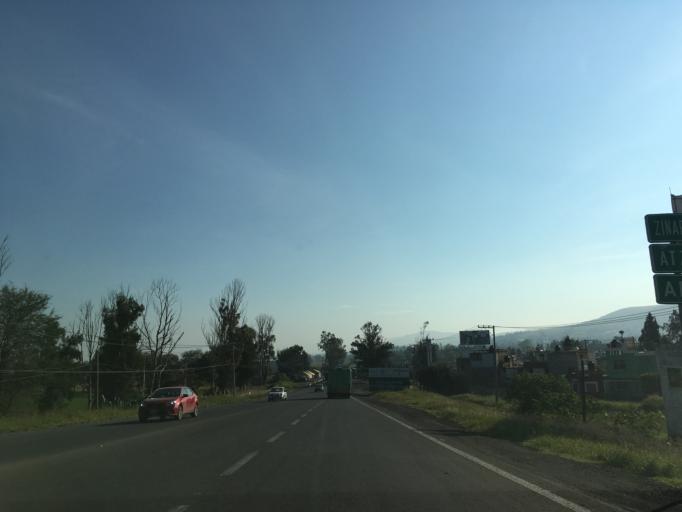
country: MX
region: Michoacan
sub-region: Tarimbaro
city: Conjunto Habitacional el Trebol
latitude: 19.7685
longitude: -101.1564
